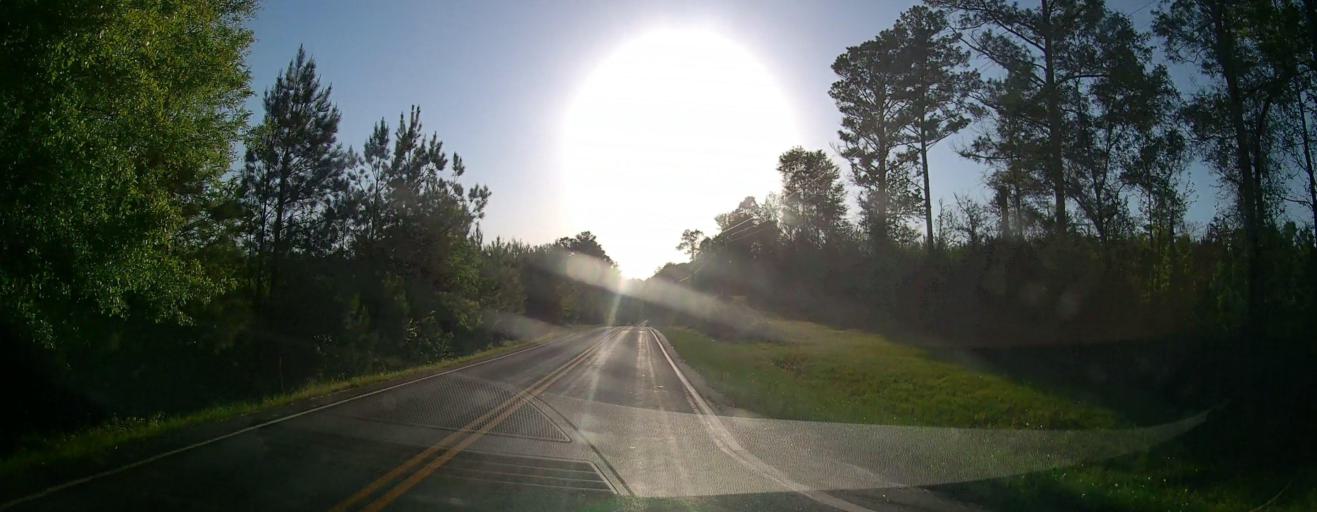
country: US
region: Georgia
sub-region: Macon County
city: Oglethorpe
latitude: 32.3175
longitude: -84.1763
